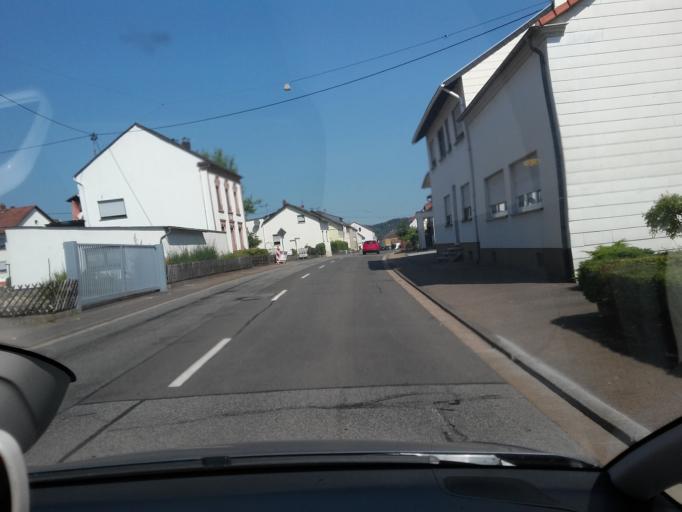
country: DE
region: Saarland
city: Mettlach
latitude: 49.4623
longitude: 6.5951
